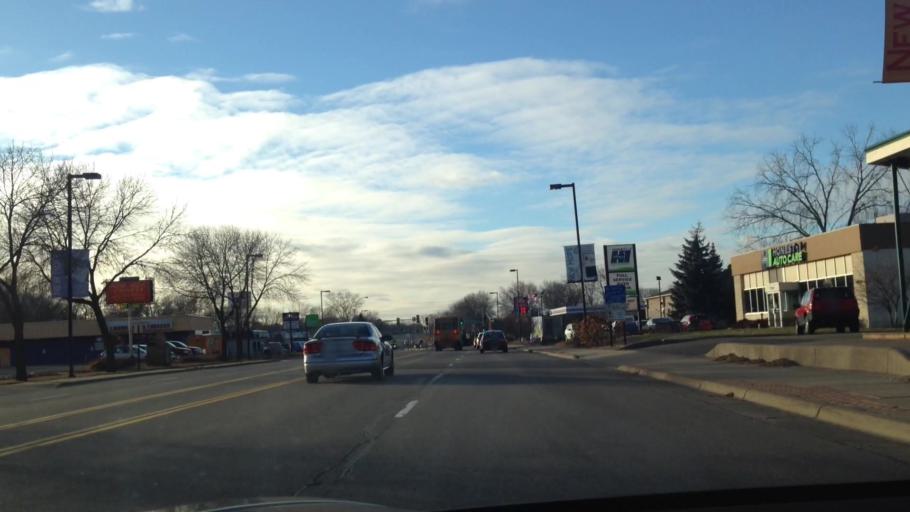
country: US
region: Minnesota
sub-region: Hennepin County
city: Crystal
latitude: 45.0329
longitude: -93.3704
